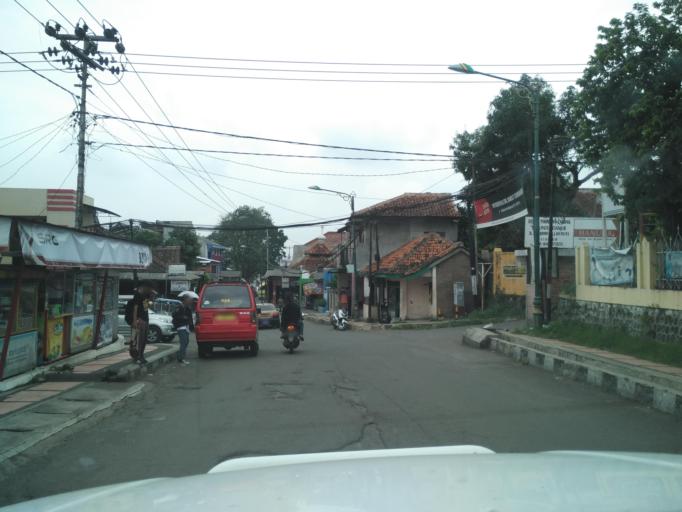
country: ID
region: West Java
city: Ciranjang-hilir
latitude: -6.8260
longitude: 107.1325
